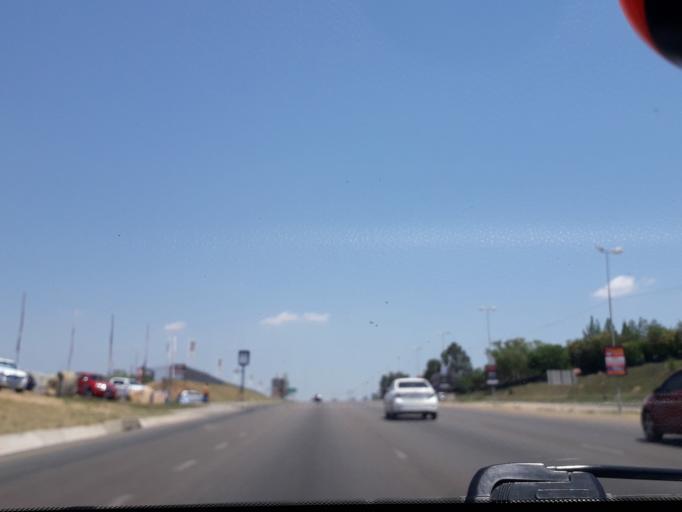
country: ZA
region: Gauteng
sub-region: City of Johannesburg Metropolitan Municipality
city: Midrand
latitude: -26.0458
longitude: 28.0907
